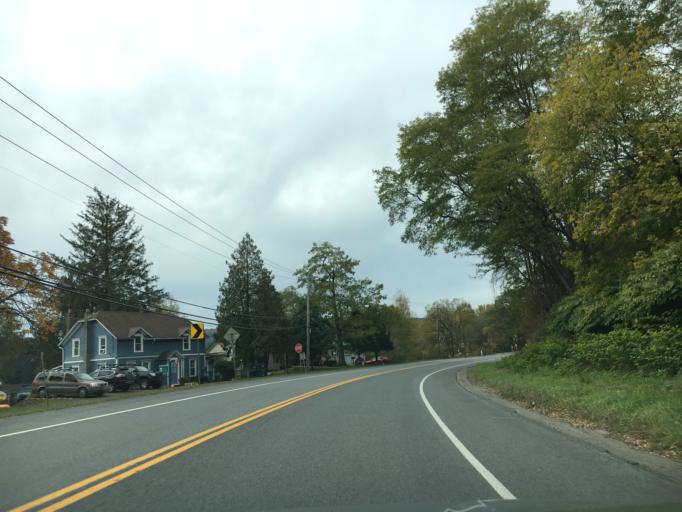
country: US
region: New York
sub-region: Otsego County
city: Oneonta
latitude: 42.5288
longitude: -74.9692
